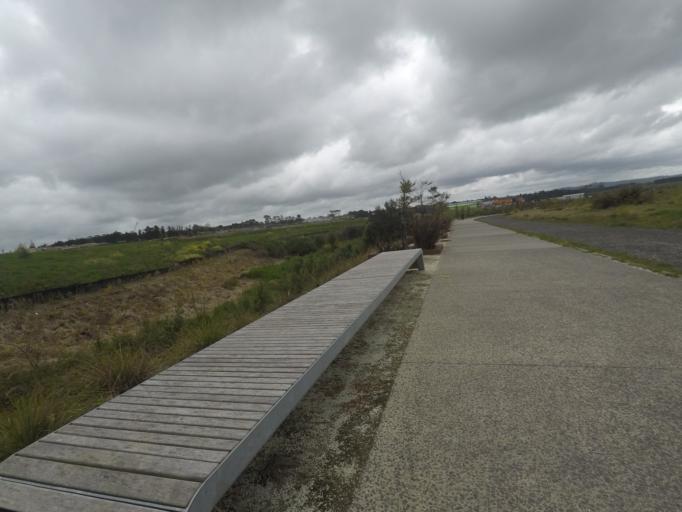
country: NZ
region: Auckland
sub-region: Auckland
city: Rosebank
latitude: -36.8149
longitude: 174.6075
